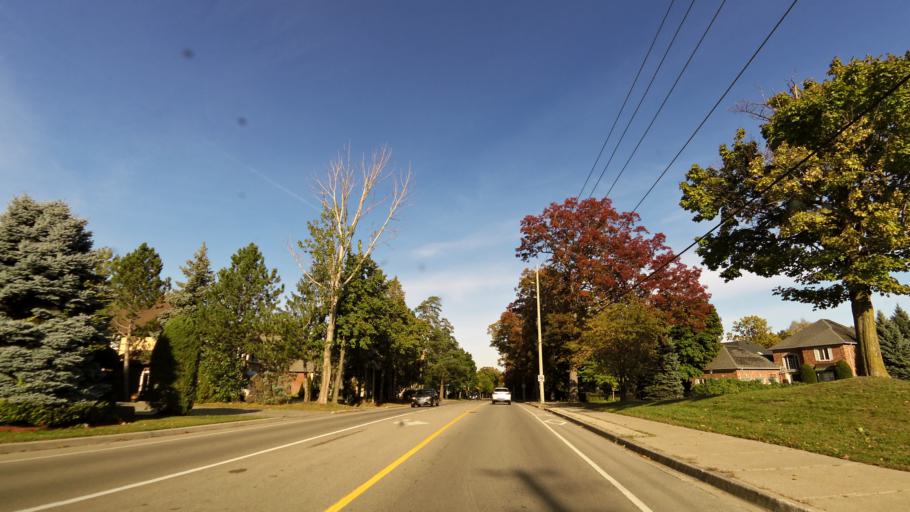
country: CA
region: Ontario
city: Mississauga
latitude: 43.5356
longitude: -79.6475
